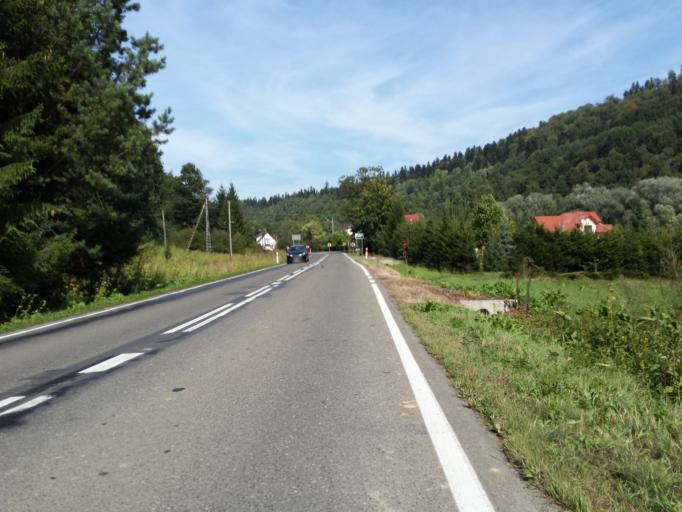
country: PL
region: Subcarpathian Voivodeship
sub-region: Powiat leski
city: Lesko
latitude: 49.4467
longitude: 22.3481
